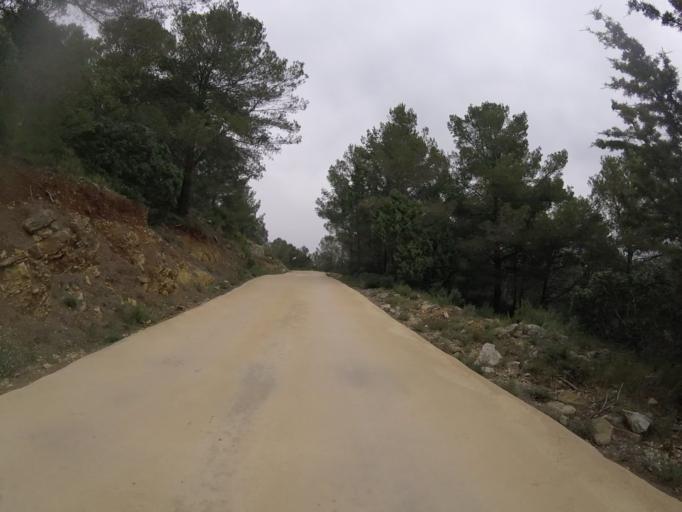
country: ES
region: Valencia
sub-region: Provincia de Castello
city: Alcala de Xivert
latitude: 40.3024
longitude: 0.2571
